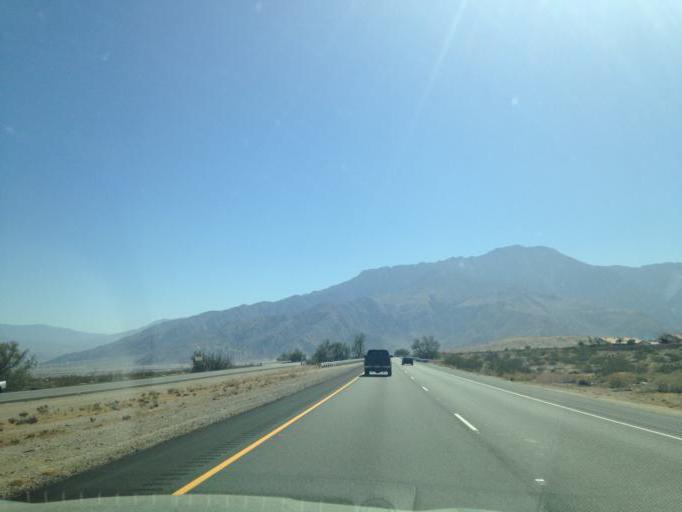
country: US
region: California
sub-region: Riverside County
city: Garnet
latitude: 33.9607
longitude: -116.5909
